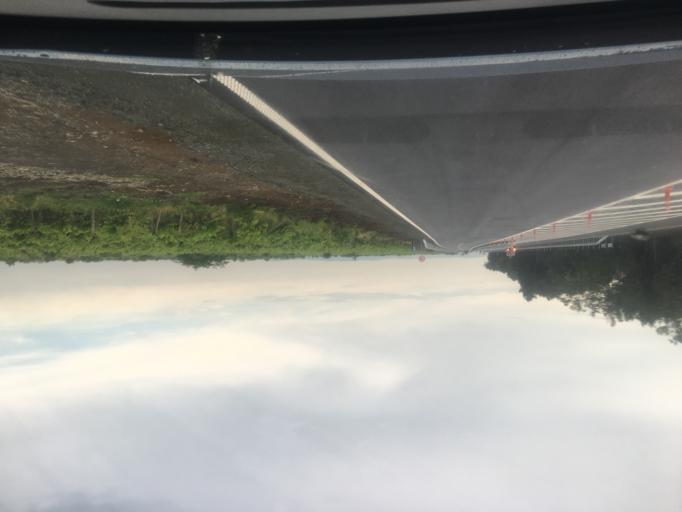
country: BG
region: Burgas
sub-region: Obshtina Pomorie
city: Pomorie
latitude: 42.5950
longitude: 27.6146
